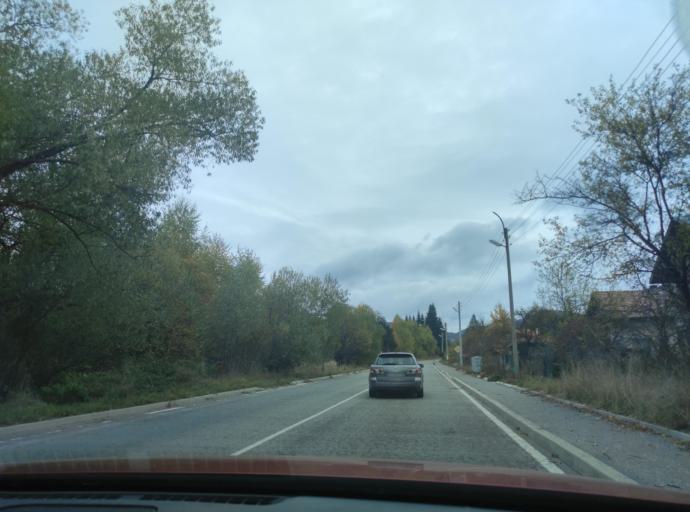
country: BG
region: Sofiya
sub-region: Obshtina Godech
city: Godech
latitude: 43.0912
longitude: 23.0981
